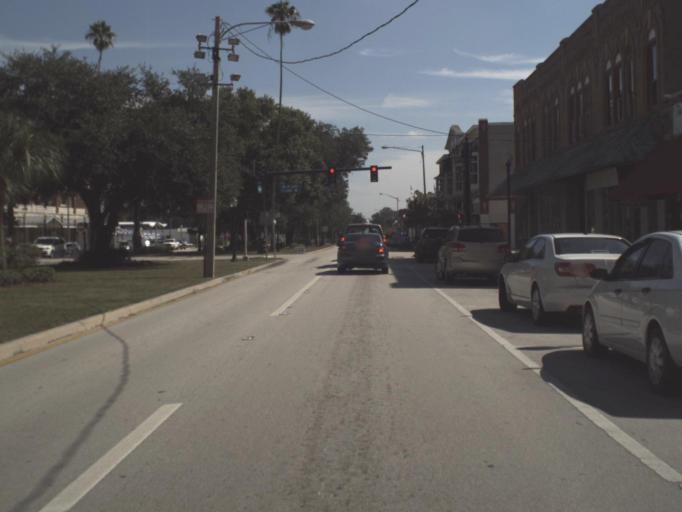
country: US
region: Florida
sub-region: Highlands County
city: Avon Park
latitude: 27.5956
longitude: -81.5029
